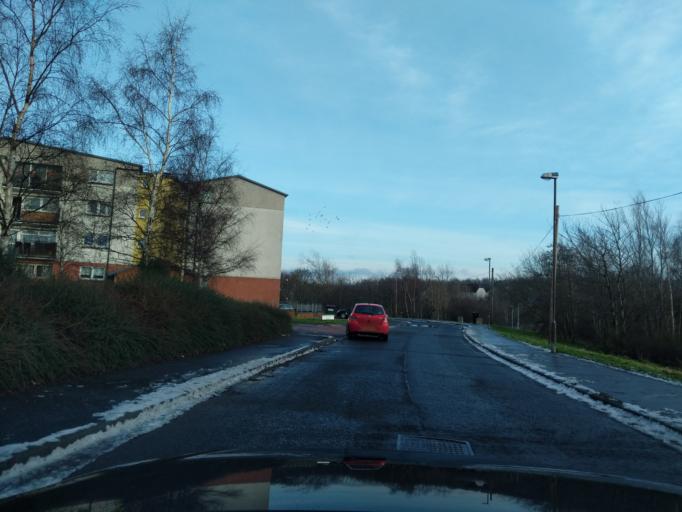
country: GB
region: Scotland
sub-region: Midlothian
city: Loanhead
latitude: 55.8991
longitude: -3.1533
